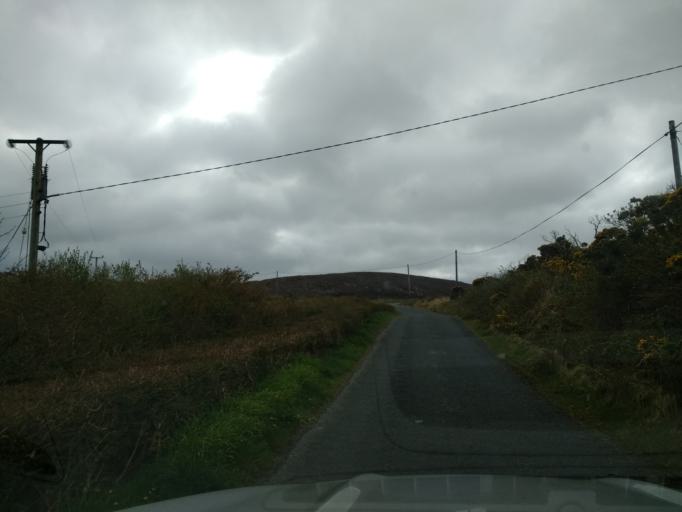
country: IE
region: Ulster
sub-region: County Donegal
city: Ramelton
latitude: 55.2642
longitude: -7.6440
